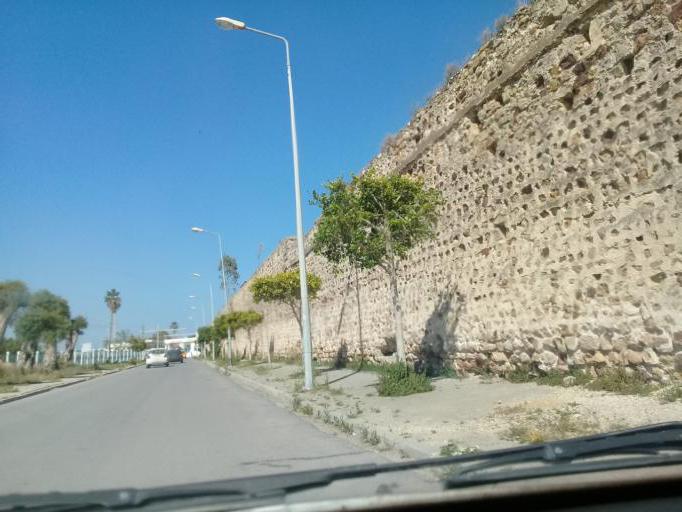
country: TN
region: Tunis
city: La Goulette
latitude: 36.8169
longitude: 10.3000
